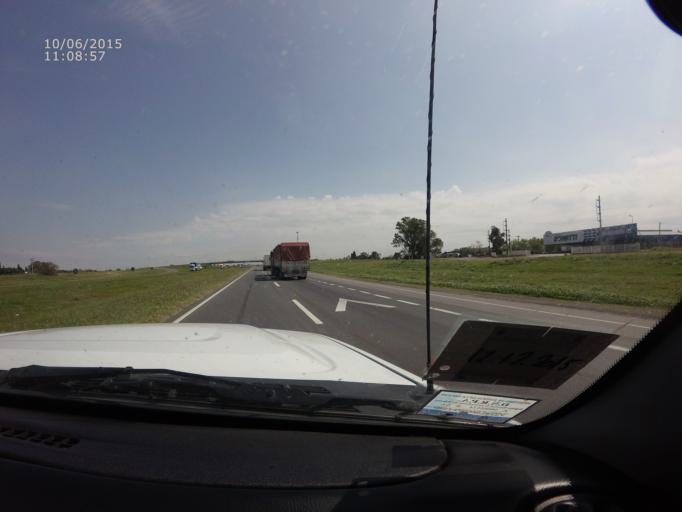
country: AR
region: Santa Fe
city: Arroyo Seco
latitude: -33.1699
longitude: -60.5281
